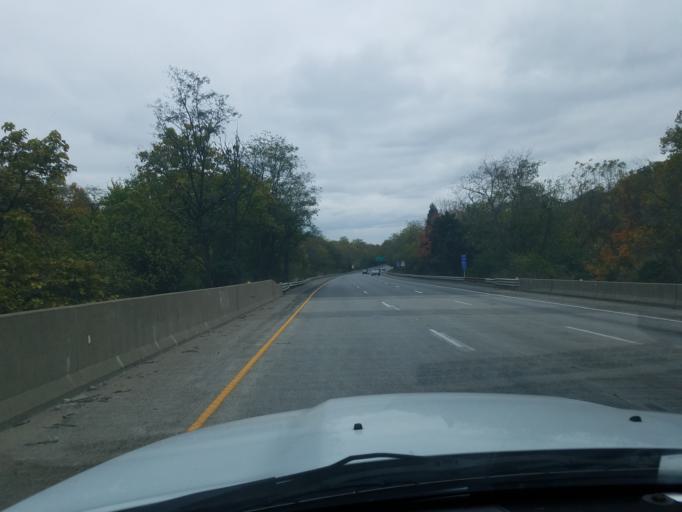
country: US
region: Indiana
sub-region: Floyd County
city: New Albany
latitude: 38.2996
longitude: -85.8471
